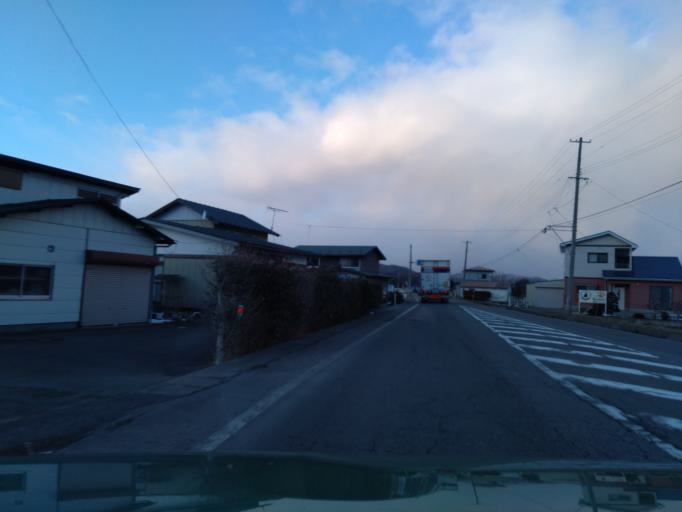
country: JP
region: Iwate
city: Shizukuishi
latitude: 39.6912
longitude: 141.0653
